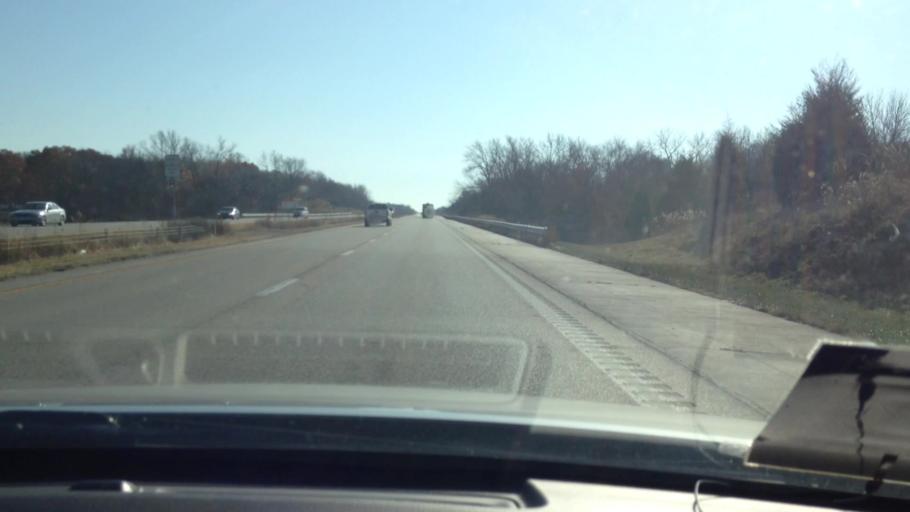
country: US
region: Missouri
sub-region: Platte County
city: Platte City
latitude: 39.4612
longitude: -94.7882
